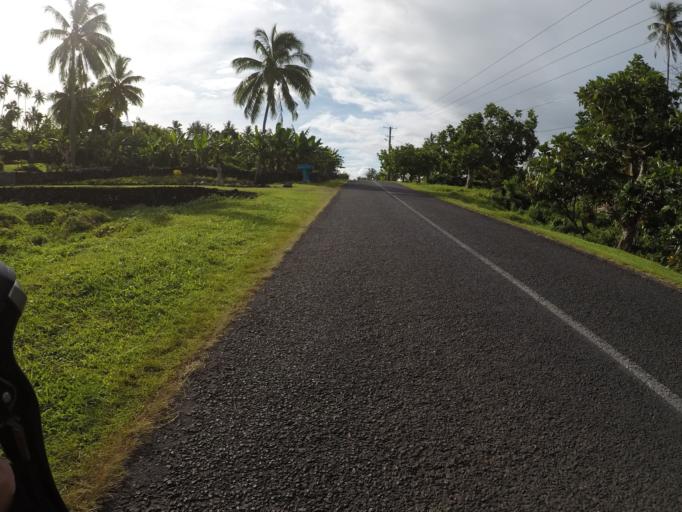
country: WS
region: Vaisigano
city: Asau
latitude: -13.6563
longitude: -172.6503
